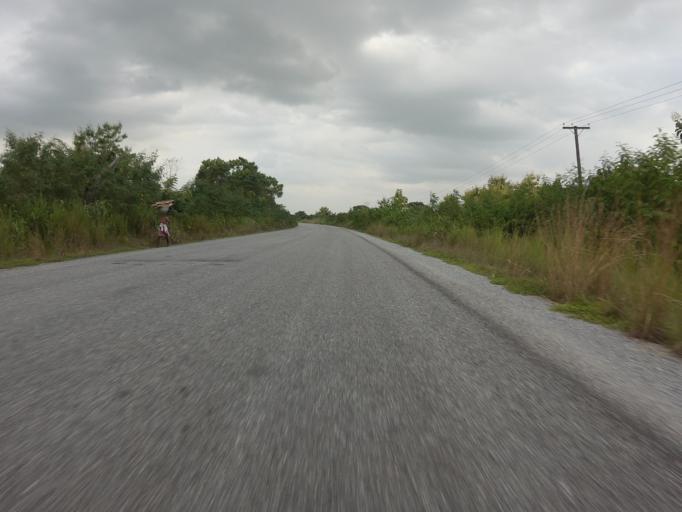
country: GH
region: Volta
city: Ho
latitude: 6.4748
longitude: 0.4956
